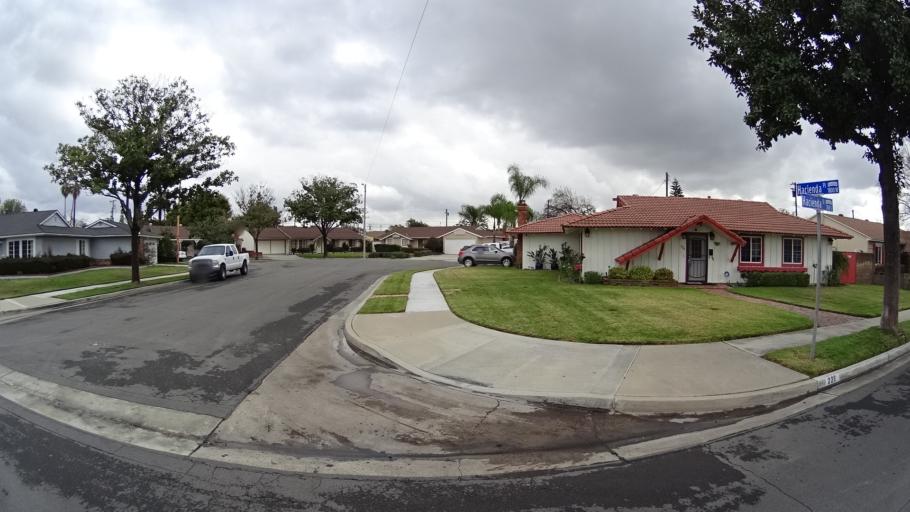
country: US
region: California
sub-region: Orange County
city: Anaheim
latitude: 33.8304
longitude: -117.9476
